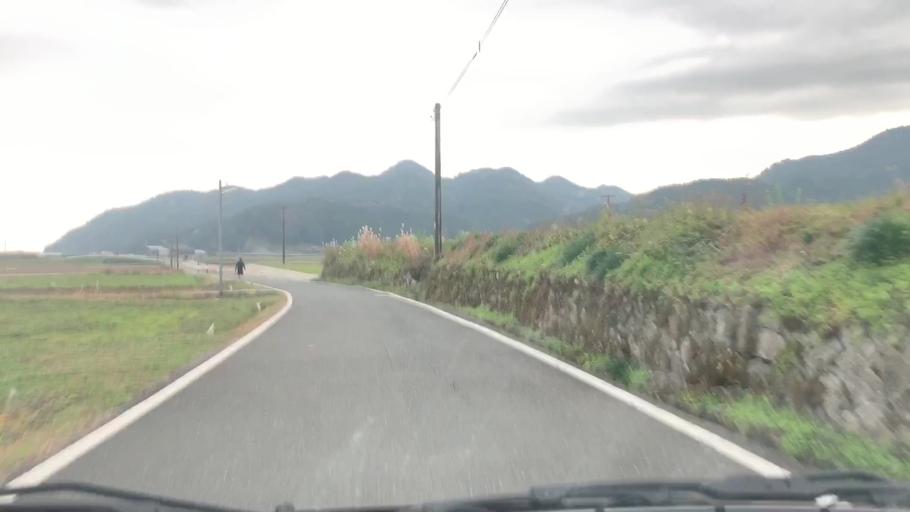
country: JP
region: Saga Prefecture
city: Ureshinomachi-shimojuku
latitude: 33.1274
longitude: 130.0306
